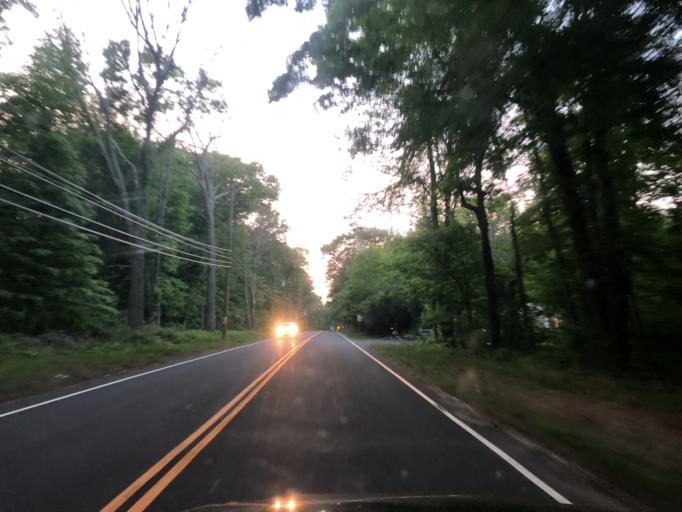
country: US
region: Connecticut
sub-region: New Haven County
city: Madison
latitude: 41.3756
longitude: -72.5654
